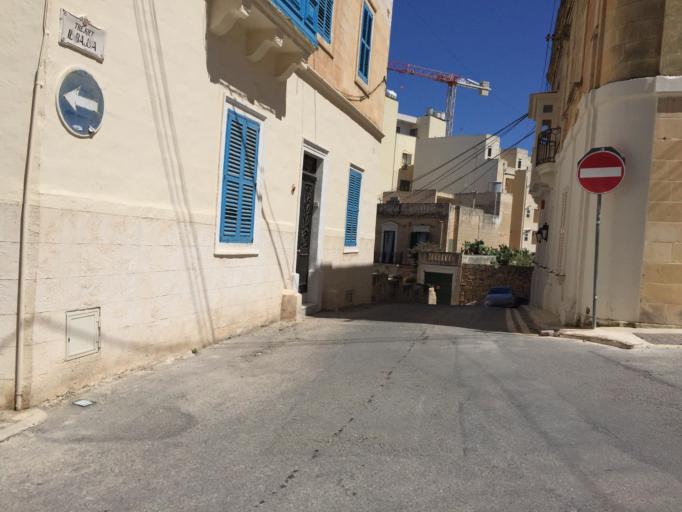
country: MT
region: Saint Julian
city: San Giljan
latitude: 35.9152
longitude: 14.4918
